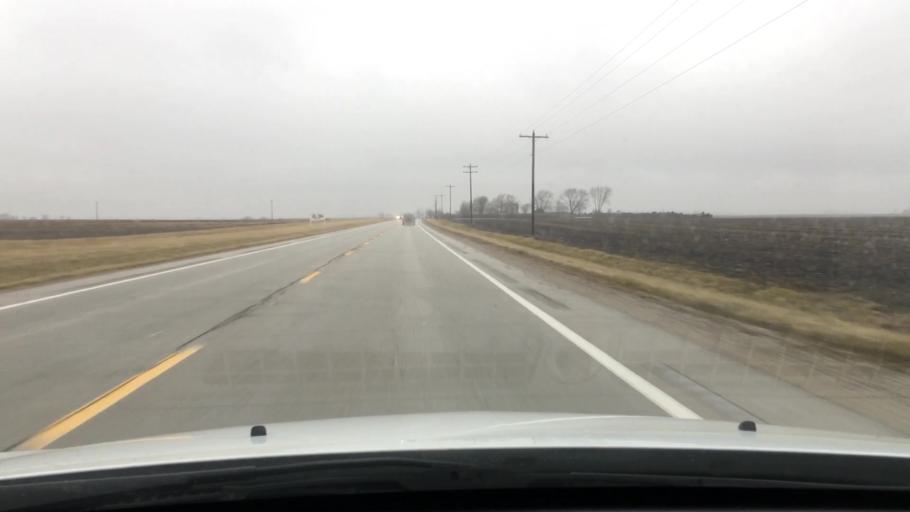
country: US
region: Illinois
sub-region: Livingston County
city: Flanagan
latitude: 40.8718
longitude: -88.8107
